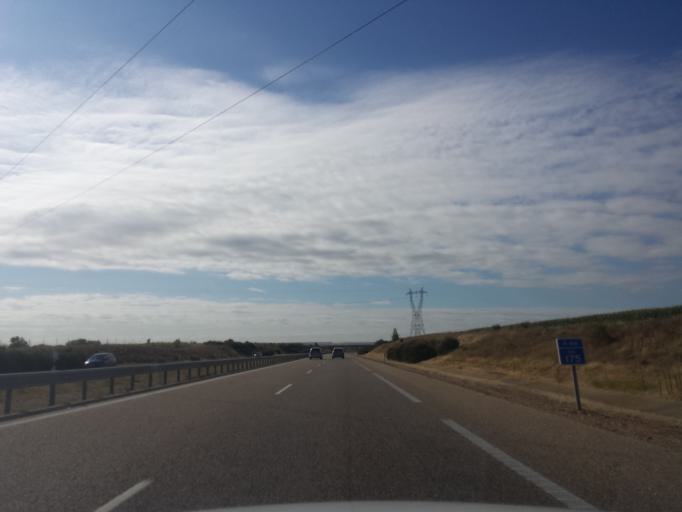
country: ES
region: Castille and Leon
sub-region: Provincia de Leon
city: Villamanan
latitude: 42.3101
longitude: -5.5982
